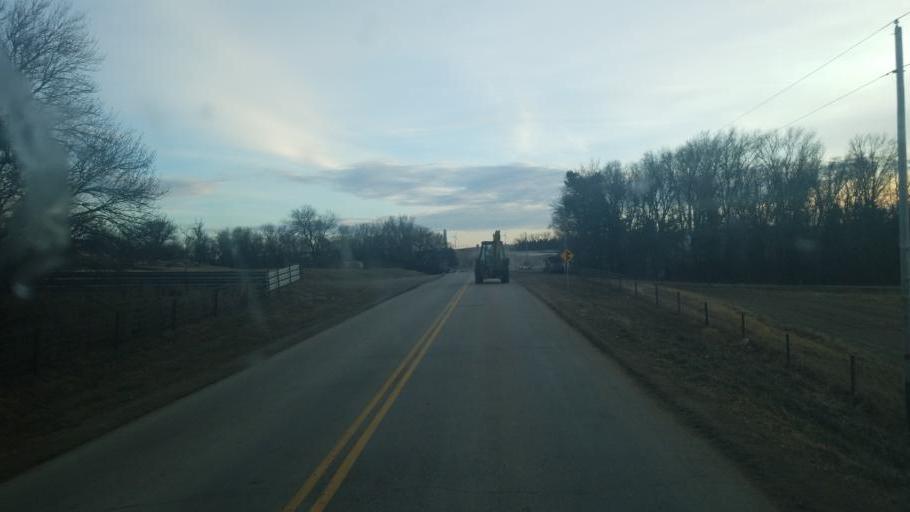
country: US
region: Nebraska
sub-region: Knox County
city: Bloomfield
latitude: 42.7030
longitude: -97.6627
